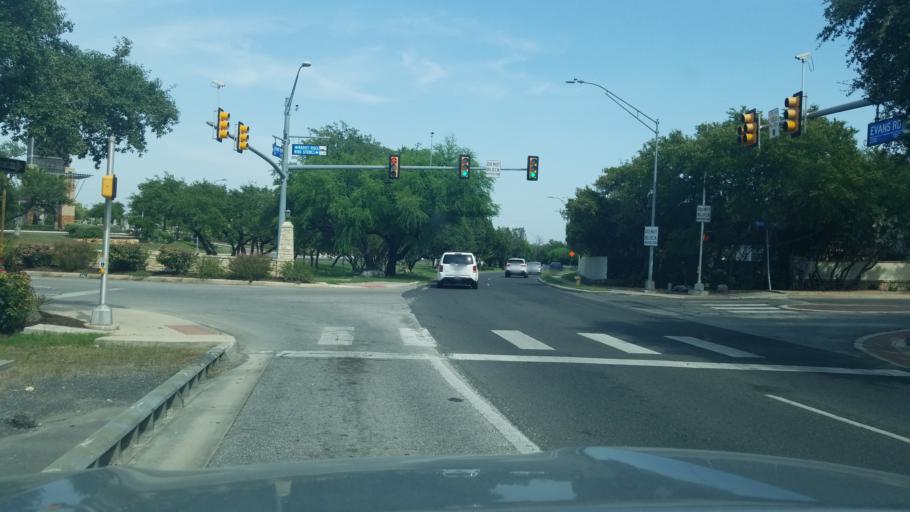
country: US
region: Texas
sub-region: Bexar County
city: Hollywood Park
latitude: 29.6386
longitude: -98.4593
